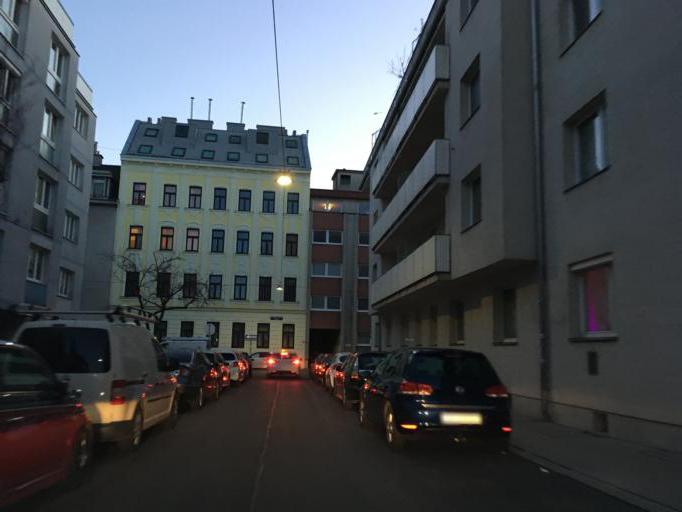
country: AT
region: Vienna
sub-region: Wien Stadt
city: Vienna
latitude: 48.2120
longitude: 16.3263
